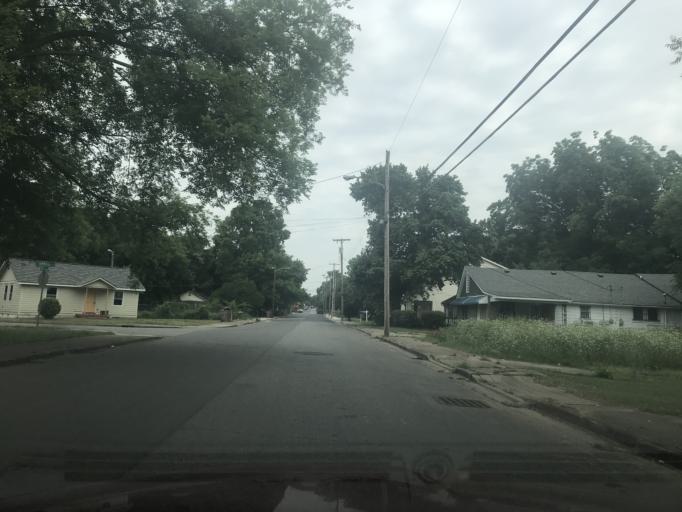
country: US
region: Tennessee
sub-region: Davidson County
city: Nashville
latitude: 36.1729
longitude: -86.8129
